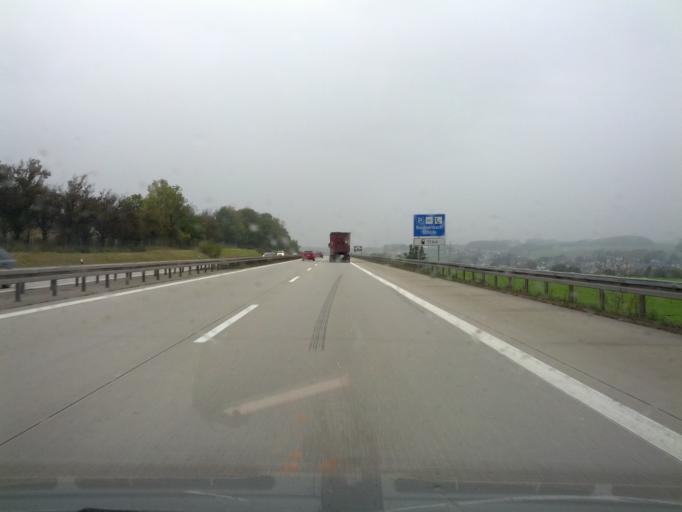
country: DE
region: Saxony
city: Stollberg
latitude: 50.6987
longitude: 12.7418
